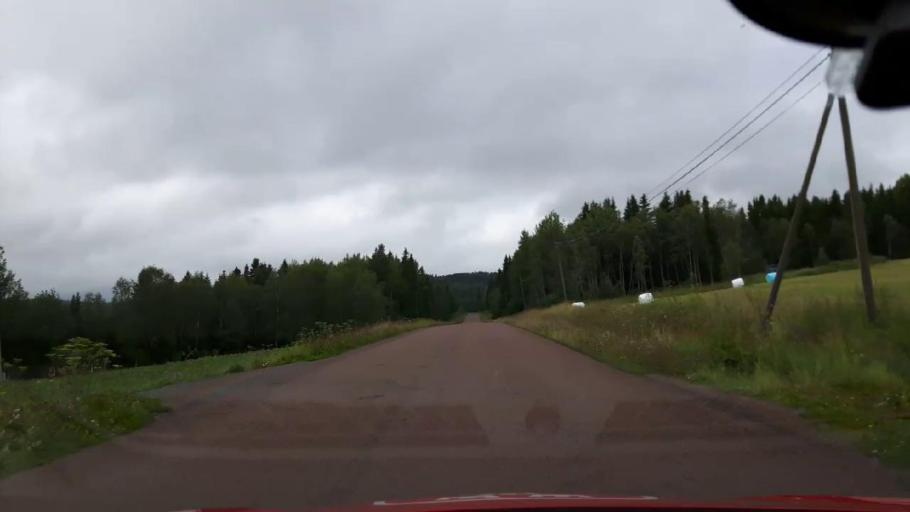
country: SE
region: Jaemtland
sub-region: Krokoms Kommun
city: Valla
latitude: 63.3898
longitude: 13.8953
